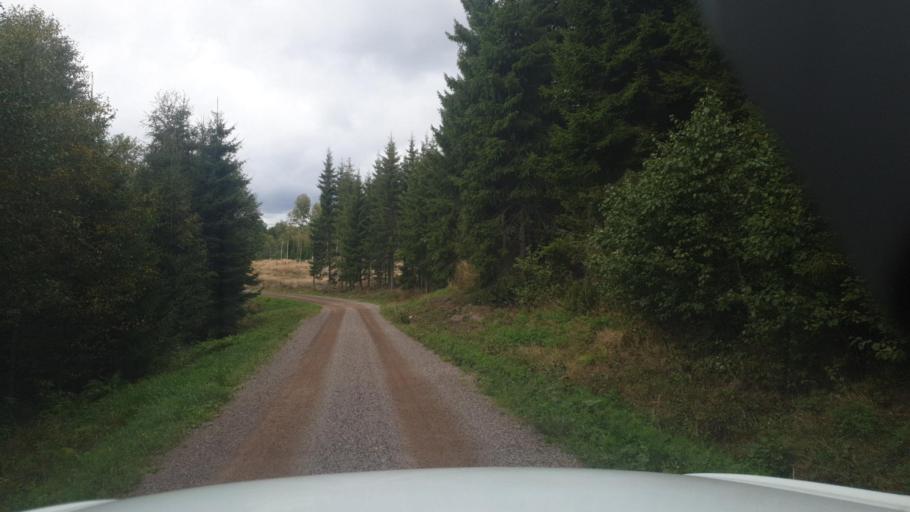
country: SE
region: Vaermland
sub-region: Torsby Kommun
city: Torsby
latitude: 59.9545
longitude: 12.7399
